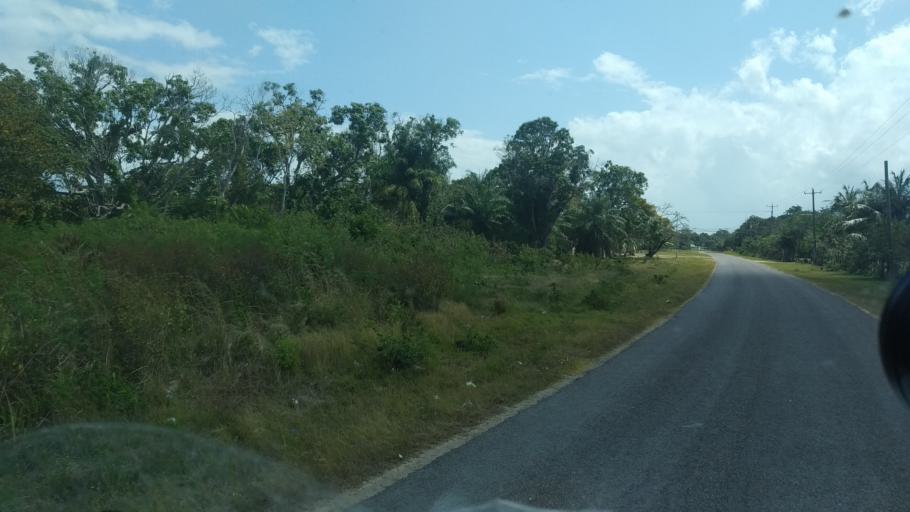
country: BZ
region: Corozal
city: Corozal
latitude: 18.3902
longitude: -88.4198
